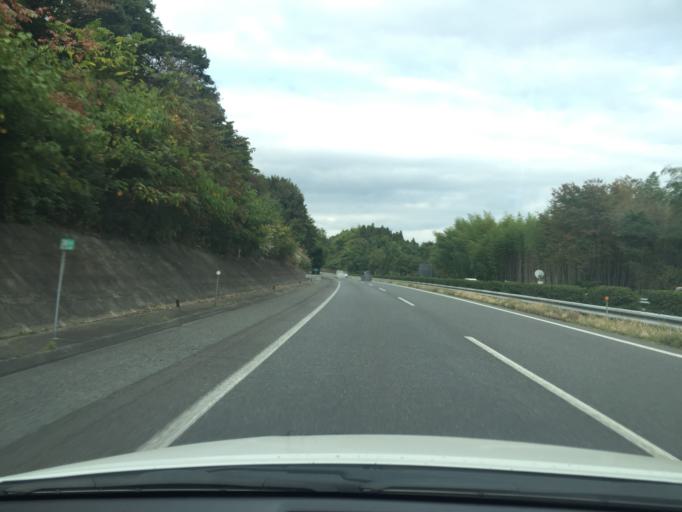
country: JP
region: Fukushima
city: Iwaki
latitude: 37.0087
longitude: 140.8135
